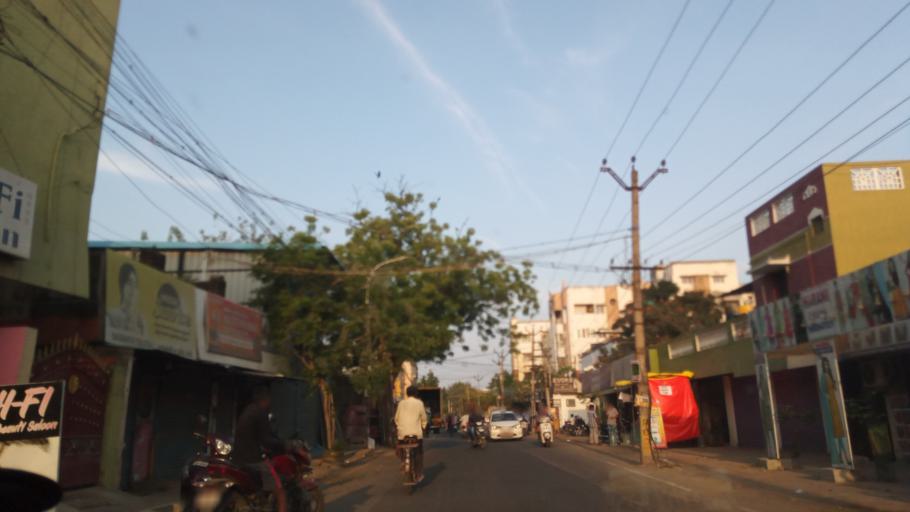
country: IN
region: Tamil Nadu
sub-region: Kancheepuram
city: Manappakkam
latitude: 13.0316
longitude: 80.1874
